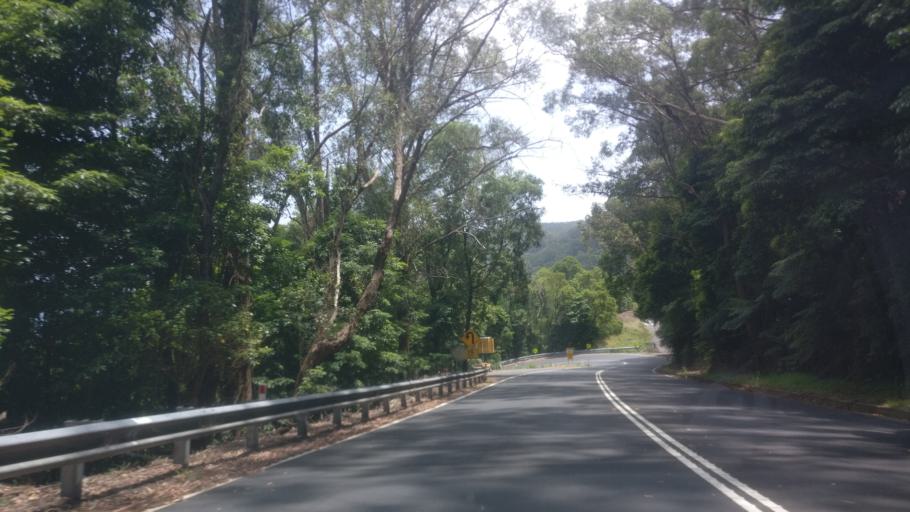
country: AU
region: New South Wales
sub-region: Shoalhaven Shire
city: Kangaroo Valley
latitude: -34.7906
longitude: 150.5599
